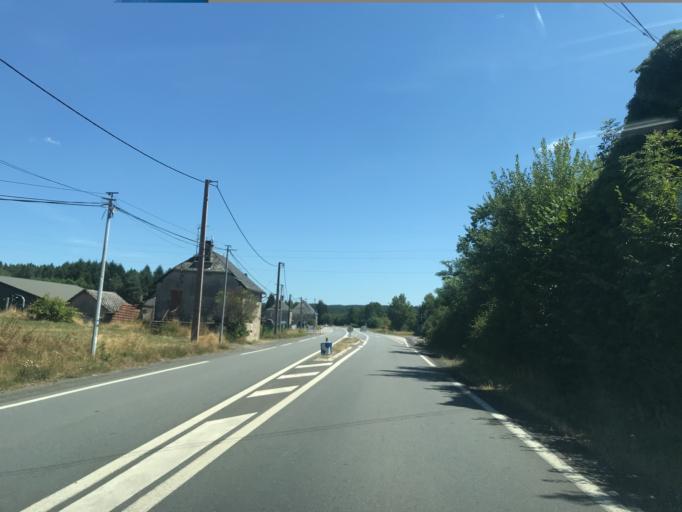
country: FR
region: Limousin
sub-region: Departement de la Correze
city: Correze
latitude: 45.3342
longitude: 1.9126
